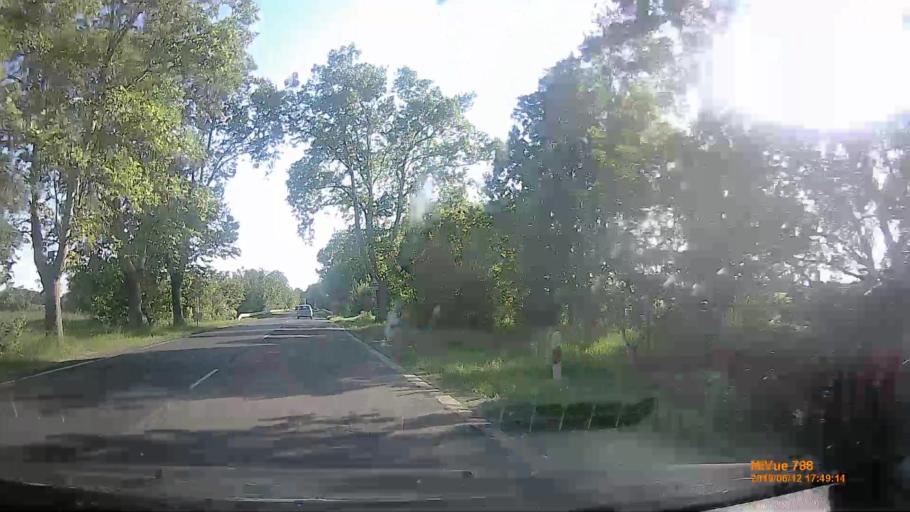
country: HU
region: Csongrad
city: Roszke
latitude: 46.2145
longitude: 20.0581
